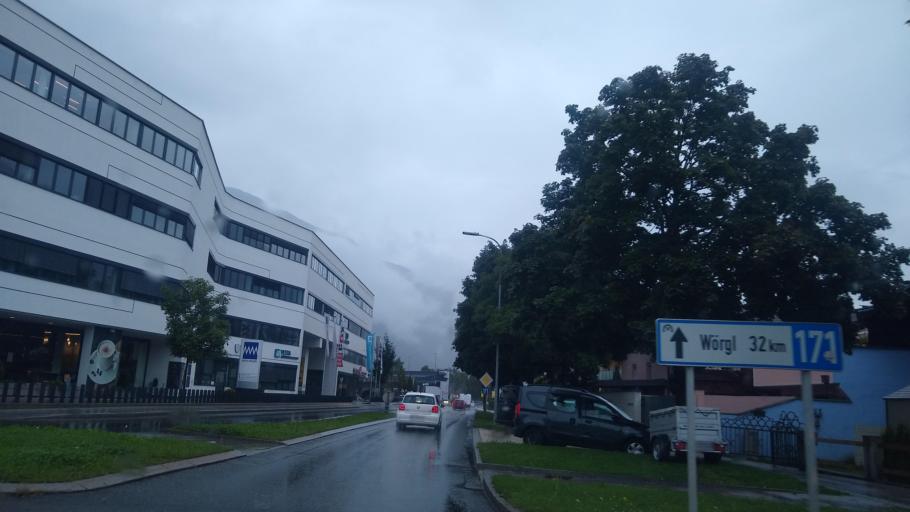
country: AT
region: Tyrol
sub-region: Politischer Bezirk Schwaz
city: Schwaz
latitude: 47.3519
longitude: 11.7064
